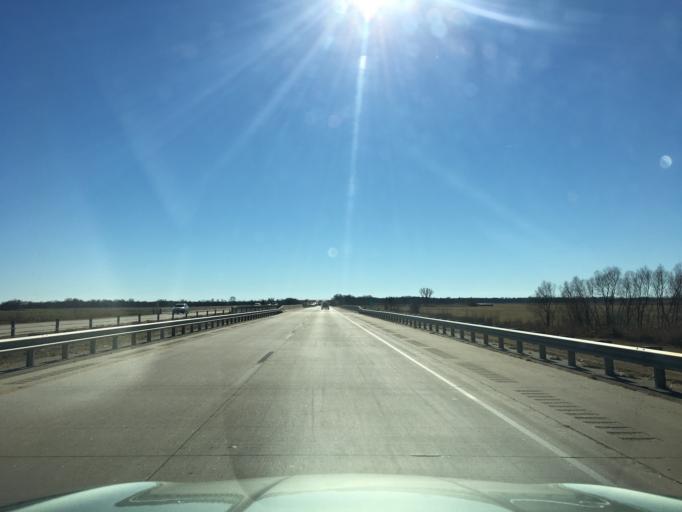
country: US
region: Oklahoma
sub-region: Noble County
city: Perry
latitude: 36.4719
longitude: -97.3272
